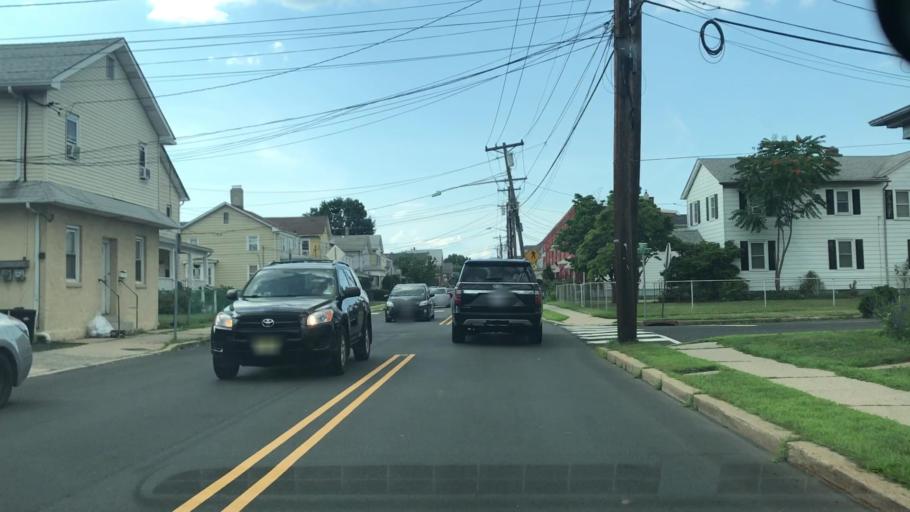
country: US
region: New Jersey
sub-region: Somerset County
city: Raritan
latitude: 40.5670
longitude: -74.6377
